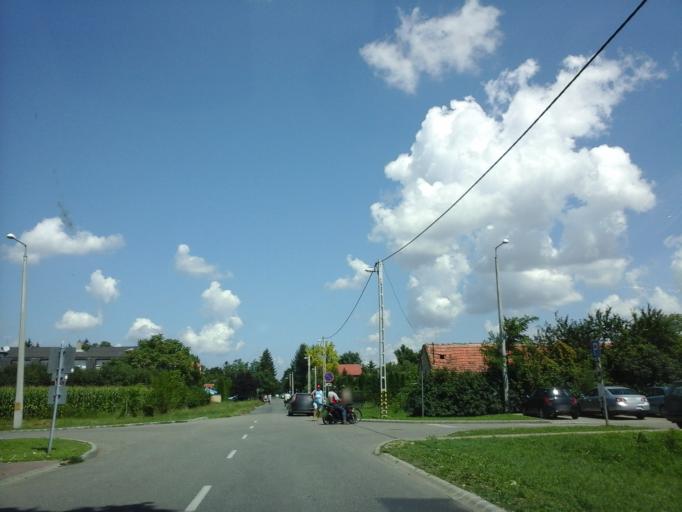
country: HU
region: Hajdu-Bihar
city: Hajduszoboszlo
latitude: 47.4548
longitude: 21.4014
